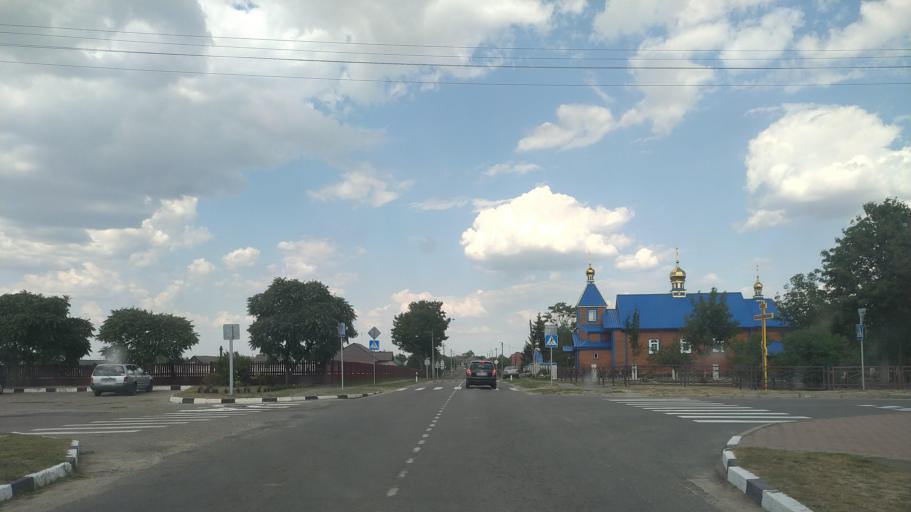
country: BY
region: Brest
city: Drahichyn
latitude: 52.1161
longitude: 25.1162
